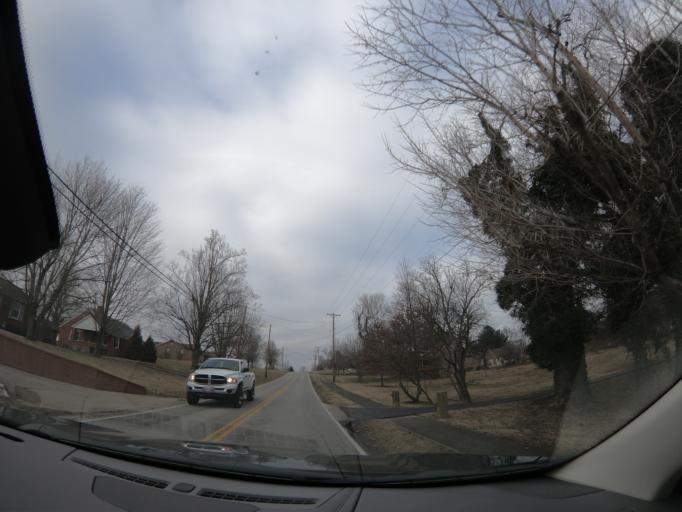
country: US
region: Kentucky
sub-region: Spencer County
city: Taylorsville
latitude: 37.9183
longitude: -85.3174
